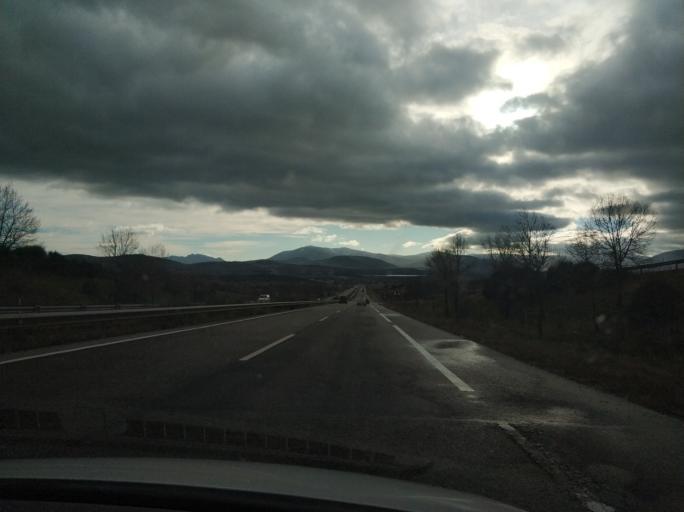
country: ES
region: Madrid
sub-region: Provincia de Madrid
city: Gascones
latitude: 41.0271
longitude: -3.6229
